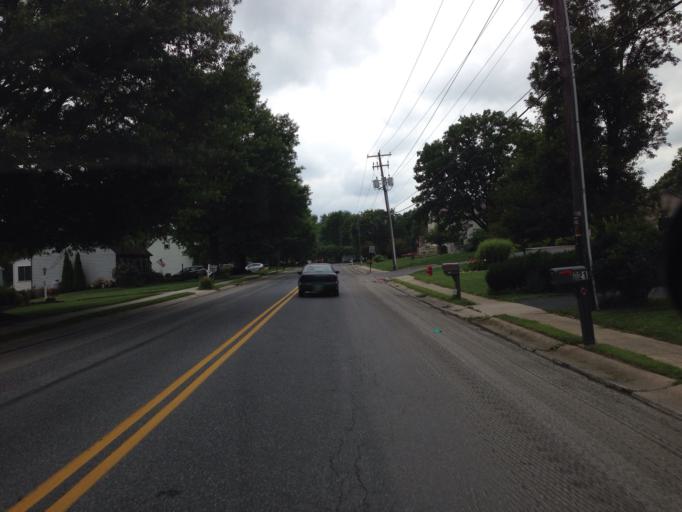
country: US
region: Pennsylvania
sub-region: Lancaster County
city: East Petersburg
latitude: 40.0877
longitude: -76.3227
